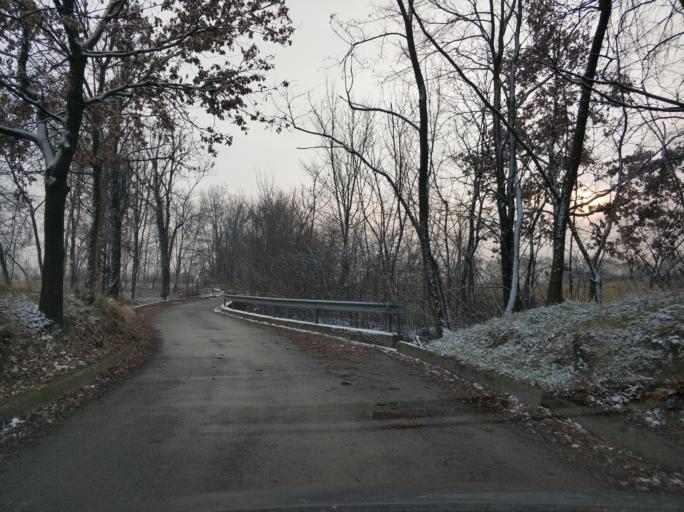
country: IT
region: Piedmont
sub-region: Provincia di Torino
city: San Francesco al Campo
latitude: 45.2220
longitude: 7.6701
